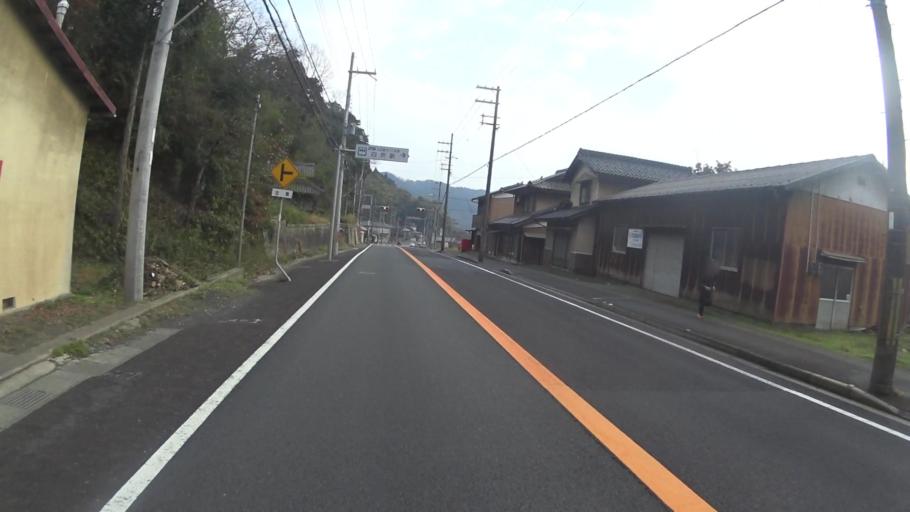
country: JP
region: Kyoto
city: Maizuru
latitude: 35.4479
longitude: 135.2895
